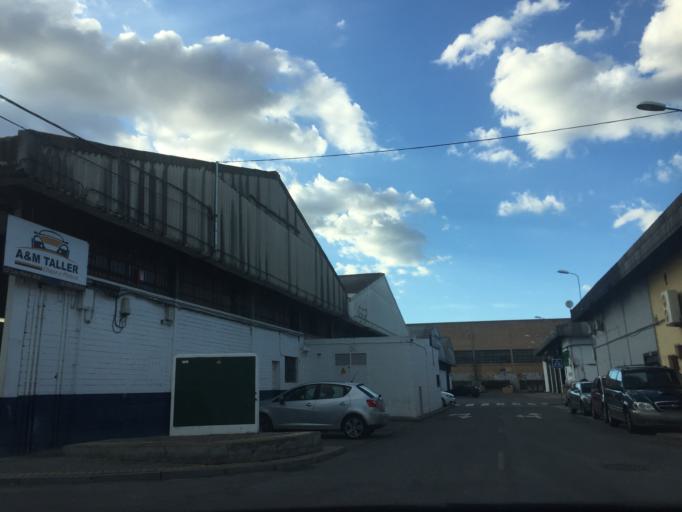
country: ES
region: Andalusia
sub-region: Provincia de Sevilla
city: Sevilla
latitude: 37.3662
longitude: -5.9592
